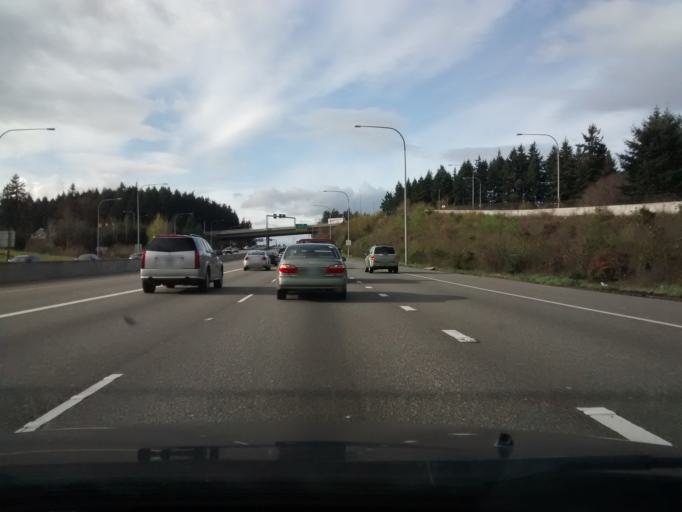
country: US
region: Washington
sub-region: Pierce County
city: Fircrest
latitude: 47.2403
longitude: -122.5022
